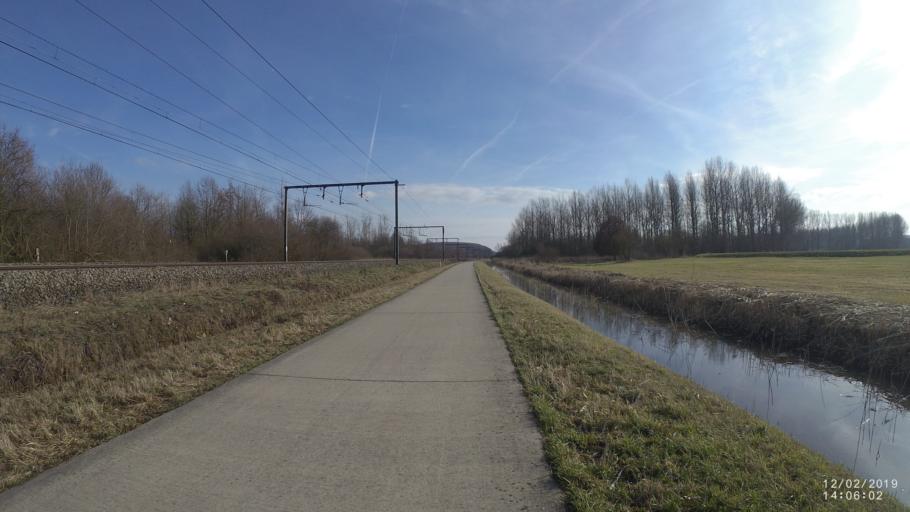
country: BE
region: Flanders
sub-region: Provincie Vlaams-Brabant
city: Scherpenheuvel-Zichem
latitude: 51.0011
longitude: 5.0017
